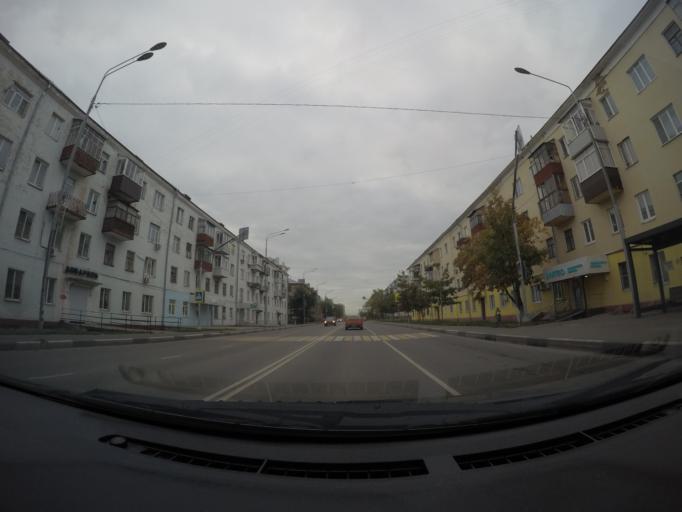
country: RU
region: Moskovskaya
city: Staraya Kupavna
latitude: 55.8095
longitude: 38.1765
